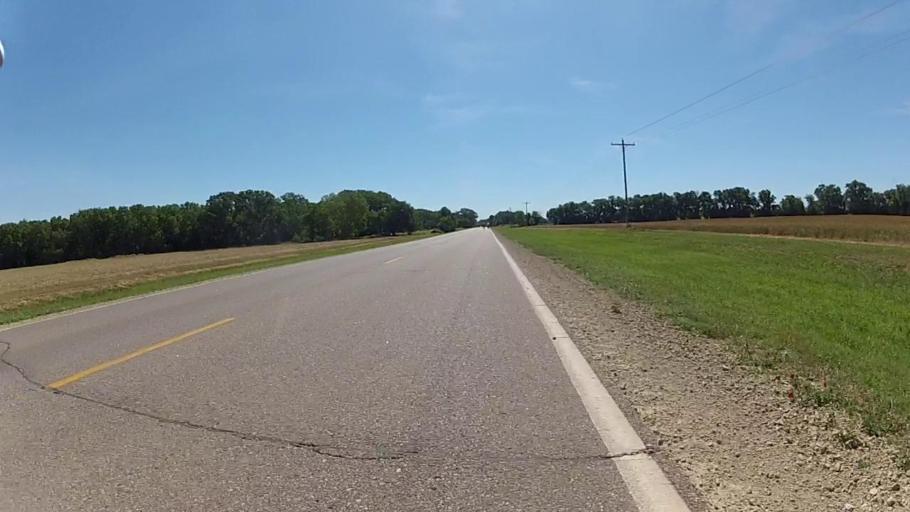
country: US
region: Kansas
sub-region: Barber County
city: Medicine Lodge
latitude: 37.2754
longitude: -98.6106
